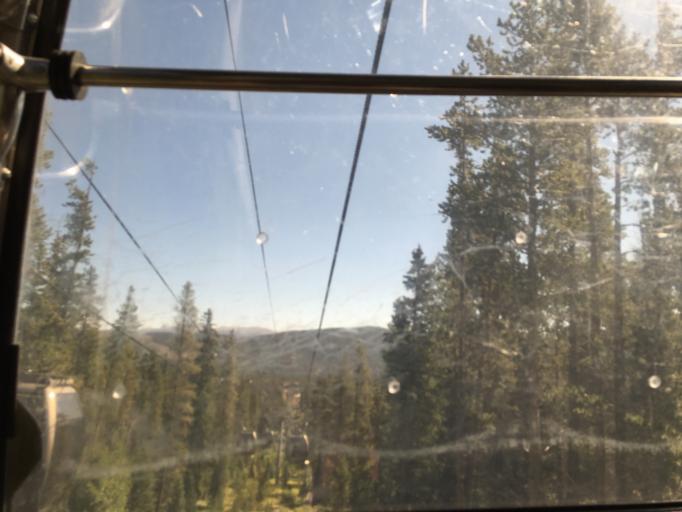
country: US
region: Colorado
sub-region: Summit County
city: Breckenridge
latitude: 39.4858
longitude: -106.0642
